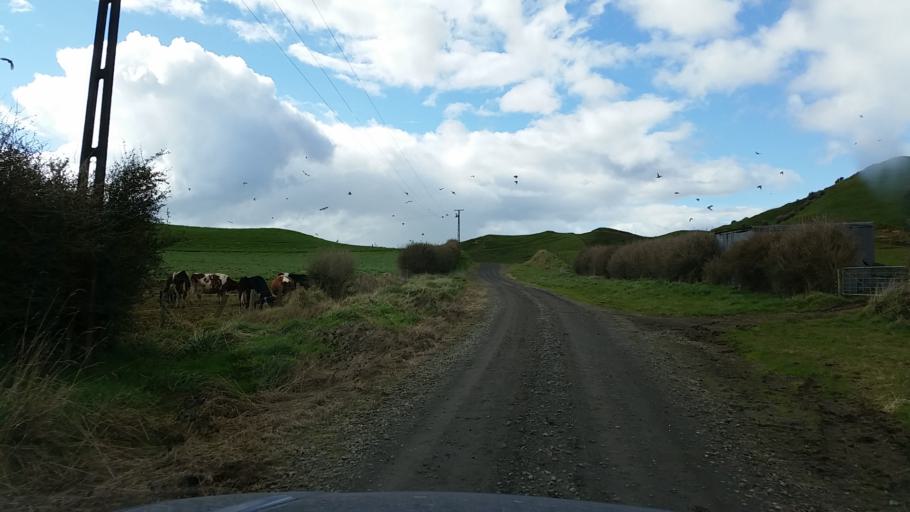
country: NZ
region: Taranaki
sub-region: South Taranaki District
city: Eltham
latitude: -39.3559
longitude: 174.3830
